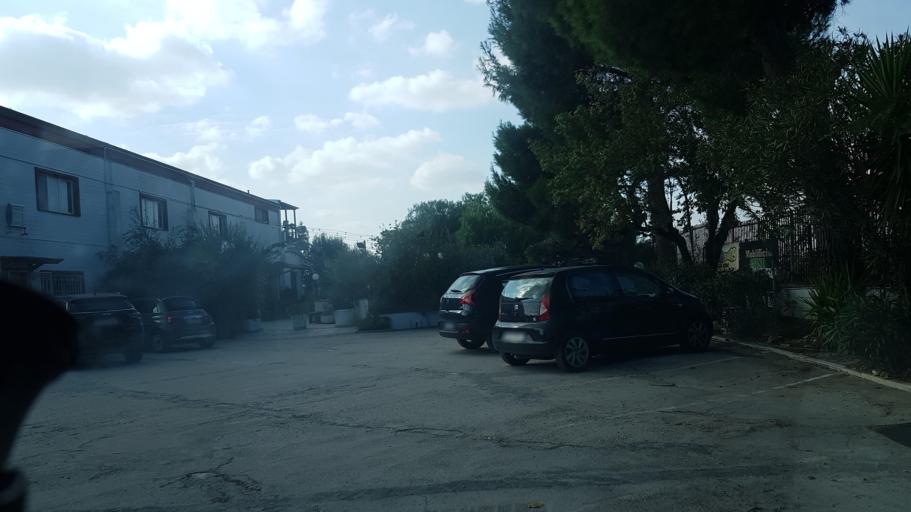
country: IT
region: Apulia
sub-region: Provincia di Foggia
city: Foggia
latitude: 41.4415
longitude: 15.5216
